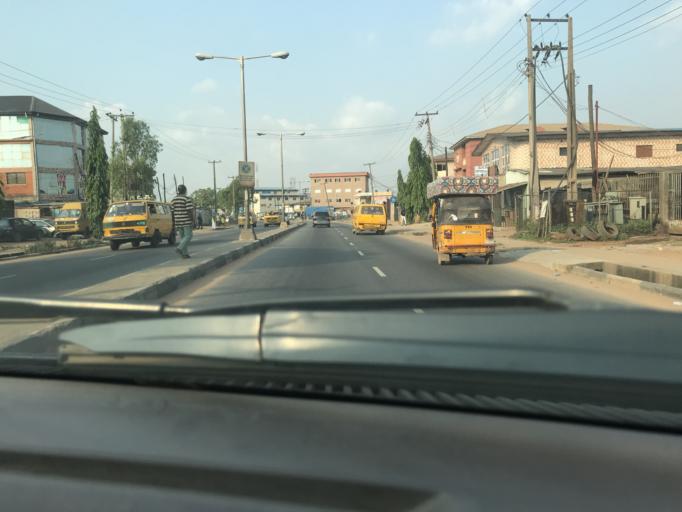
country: NG
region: Lagos
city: Agege
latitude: 6.5896
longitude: 3.2876
